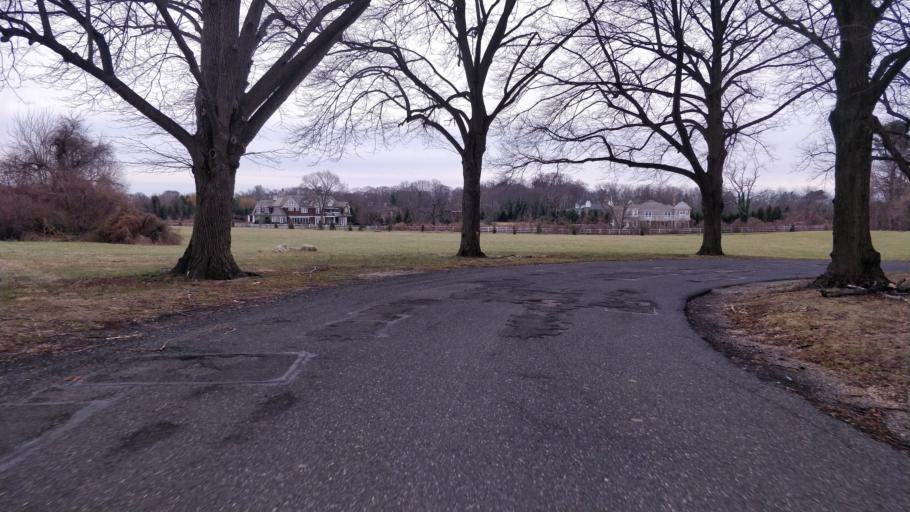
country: US
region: New York
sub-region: Nassau County
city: Old Westbury
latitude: 40.7856
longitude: -73.5757
